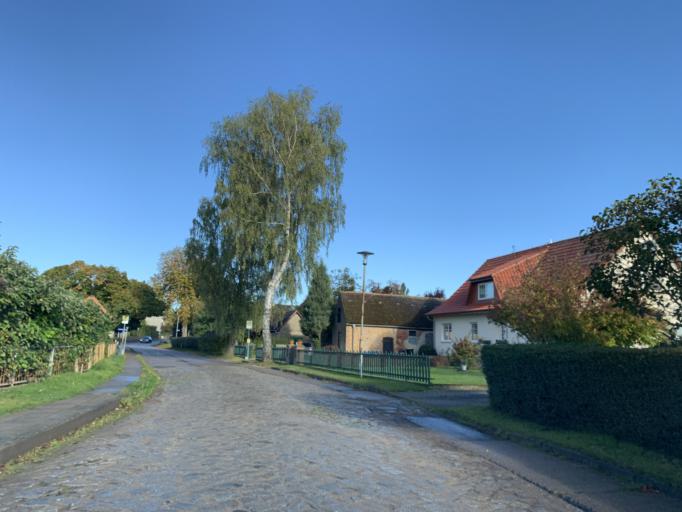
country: DE
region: Mecklenburg-Vorpommern
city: Gross Nemerow
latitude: 53.4645
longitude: 13.2729
